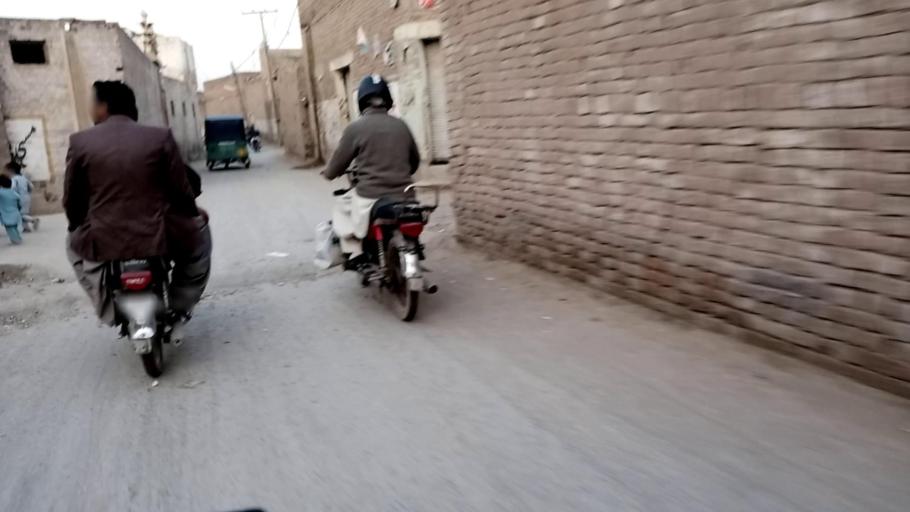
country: PK
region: Khyber Pakhtunkhwa
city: Peshawar
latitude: 34.0311
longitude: 71.4910
